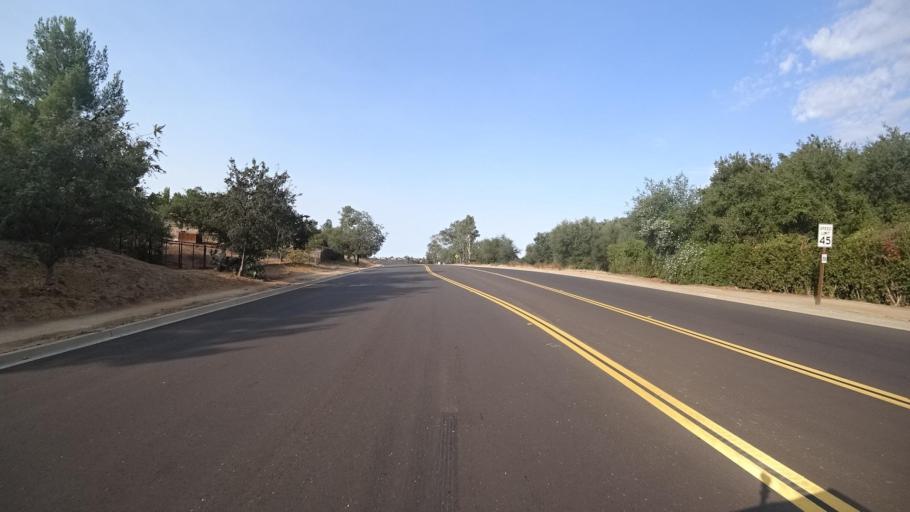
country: US
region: California
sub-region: San Diego County
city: San Diego Country Estates
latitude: 33.0065
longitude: -116.7944
